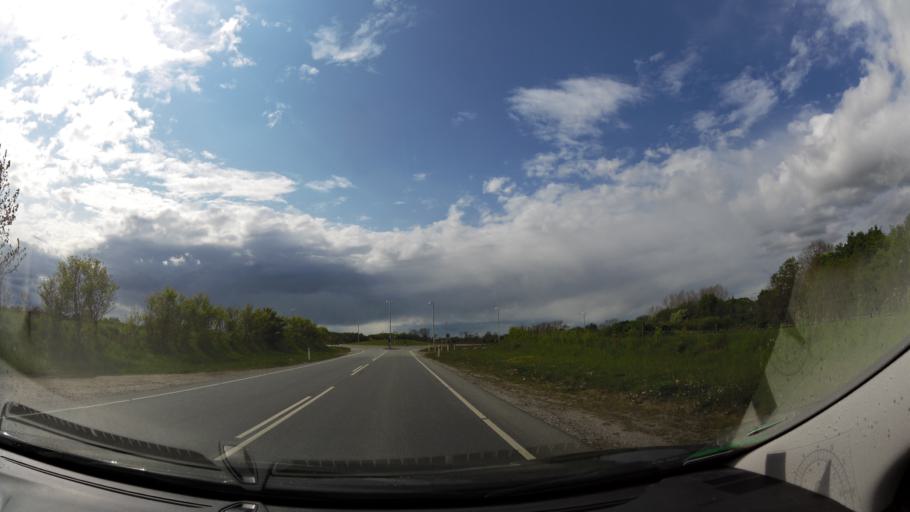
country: DK
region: South Denmark
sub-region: Nyborg Kommune
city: Nyborg
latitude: 55.3208
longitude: 10.7358
